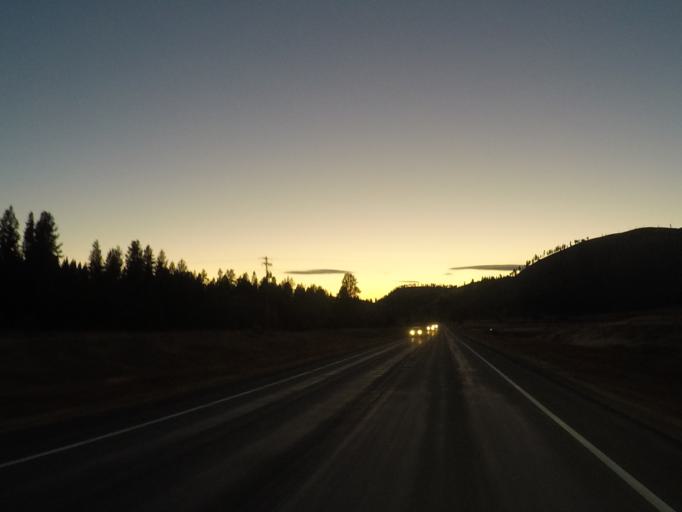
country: US
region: Montana
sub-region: Missoula County
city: Seeley Lake
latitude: 47.0306
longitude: -113.2627
